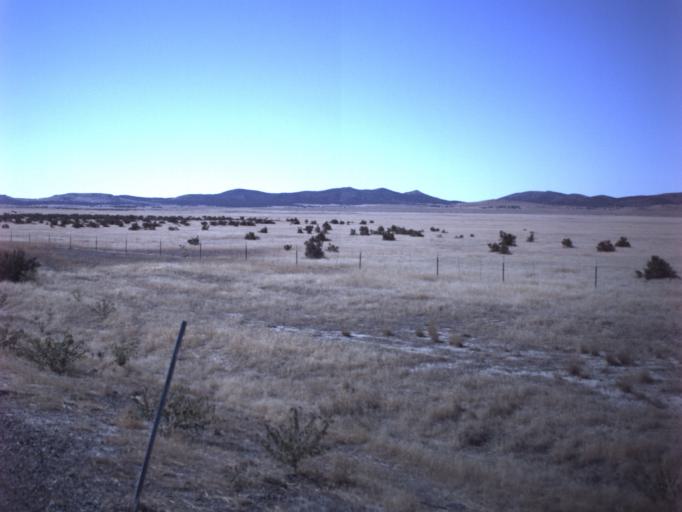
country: US
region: Utah
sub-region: Tooele County
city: Grantsville
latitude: 40.3075
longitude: -112.7432
